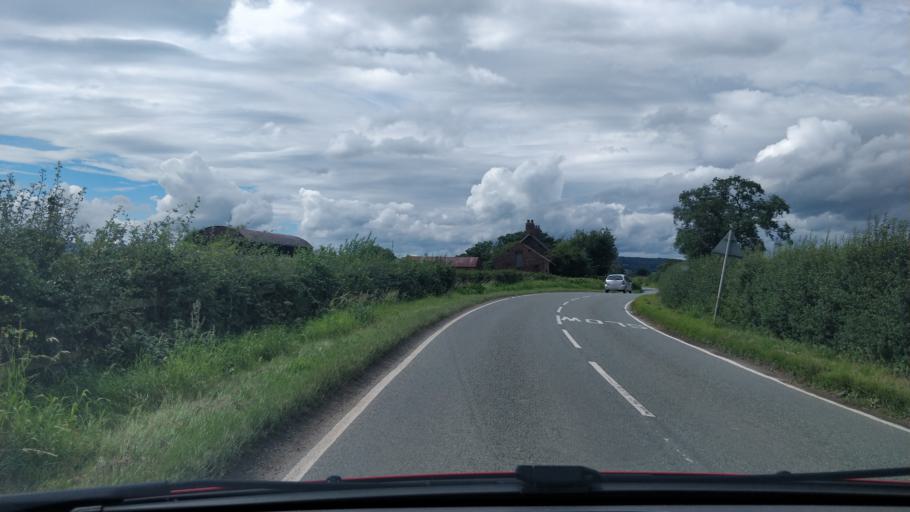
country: GB
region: Wales
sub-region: Wrexham
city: Rossett
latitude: 53.1529
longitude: -2.9648
